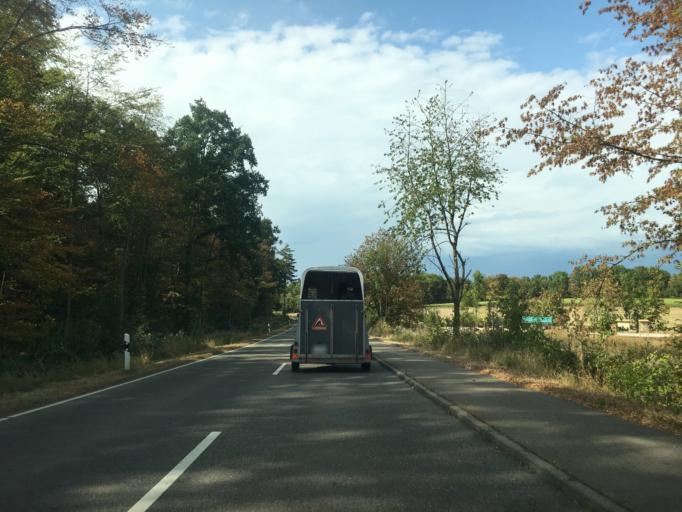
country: DE
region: Baden-Wuerttemberg
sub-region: Tuebingen Region
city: Wannweil
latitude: 48.4711
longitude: 9.1600
